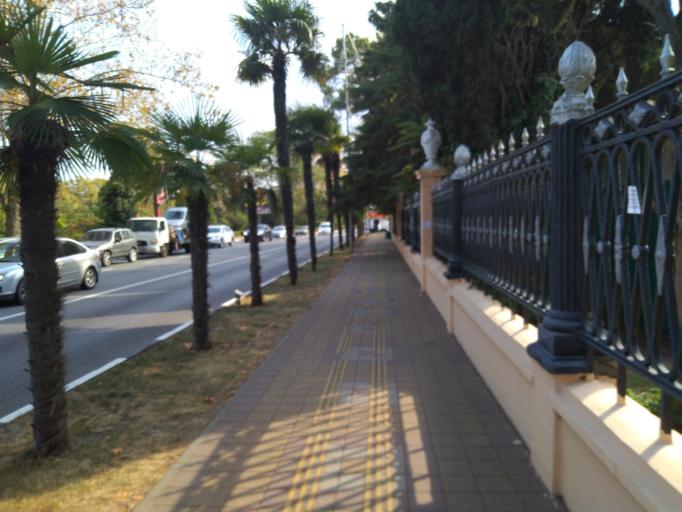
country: RU
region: Krasnodarskiy
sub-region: Sochi City
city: Sochi
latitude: 43.5914
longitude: 39.7172
